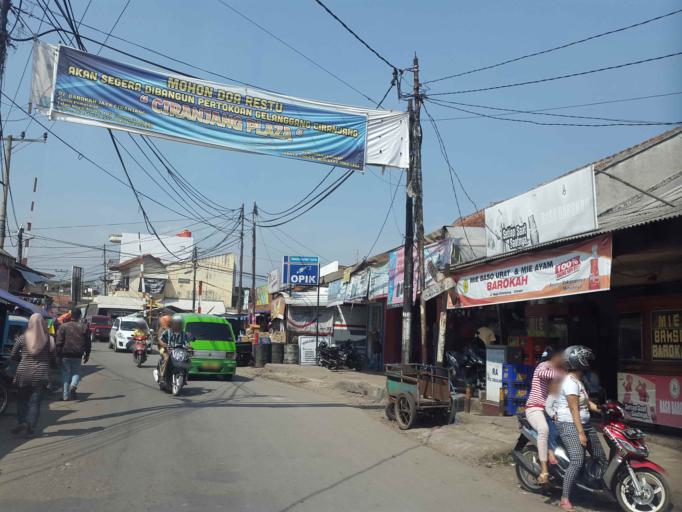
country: ID
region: West Java
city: Ciranjang-hilir
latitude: -6.8138
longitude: 107.2501
